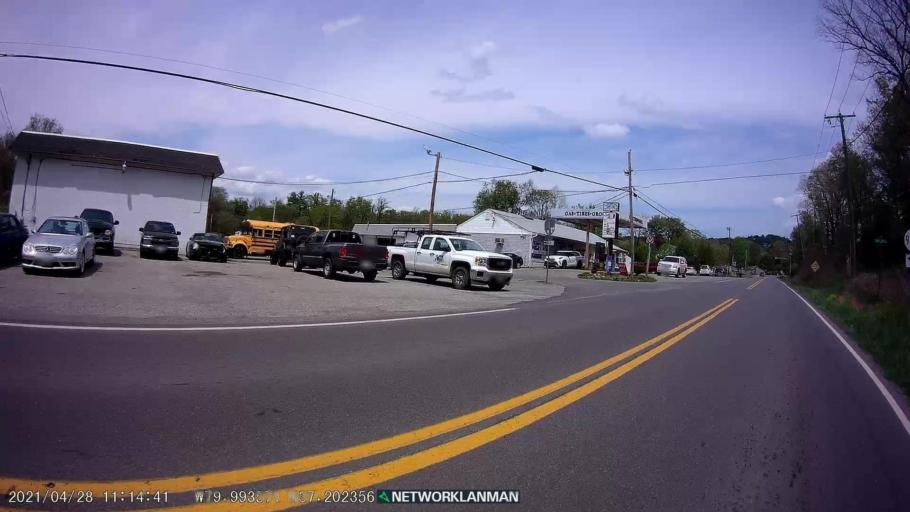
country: US
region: Virginia
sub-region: Roanoke County
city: Cave Spring
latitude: 37.2024
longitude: -79.9932
